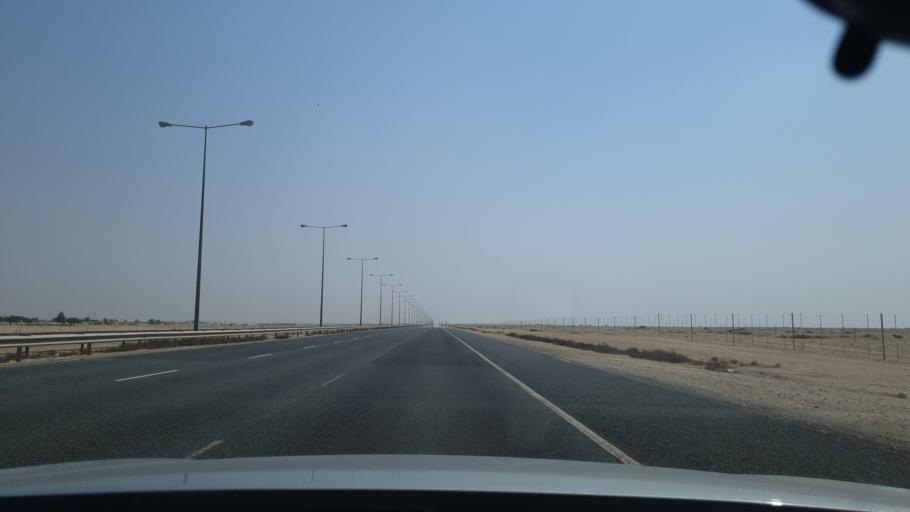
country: QA
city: Al Ghuwayriyah
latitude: 25.8143
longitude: 51.3708
